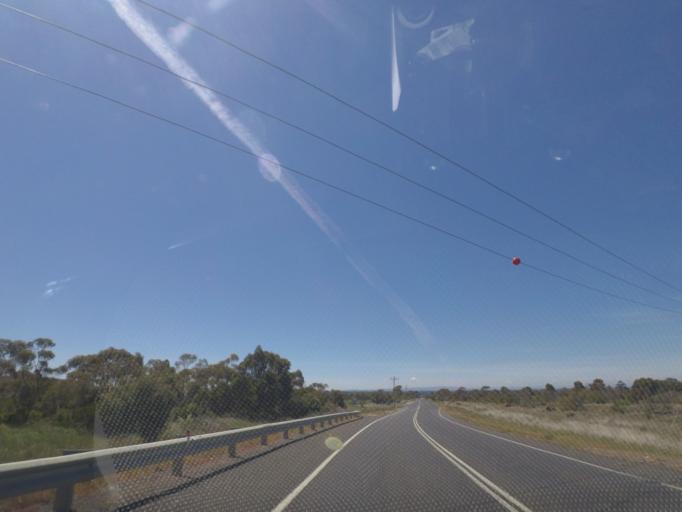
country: AU
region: Victoria
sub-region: Hume
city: Sunbury
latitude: -37.4679
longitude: 144.6528
